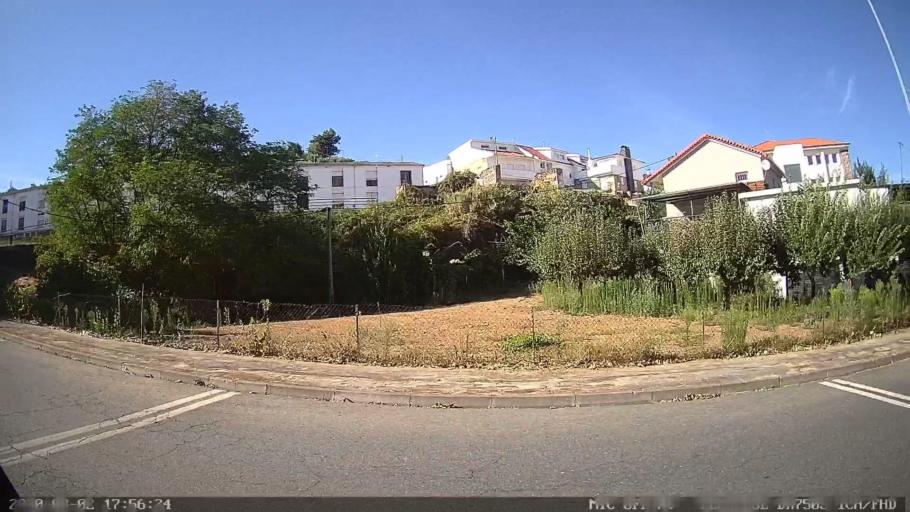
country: PT
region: Vila Real
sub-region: Murca
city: Murca
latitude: 41.4008
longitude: -7.4568
